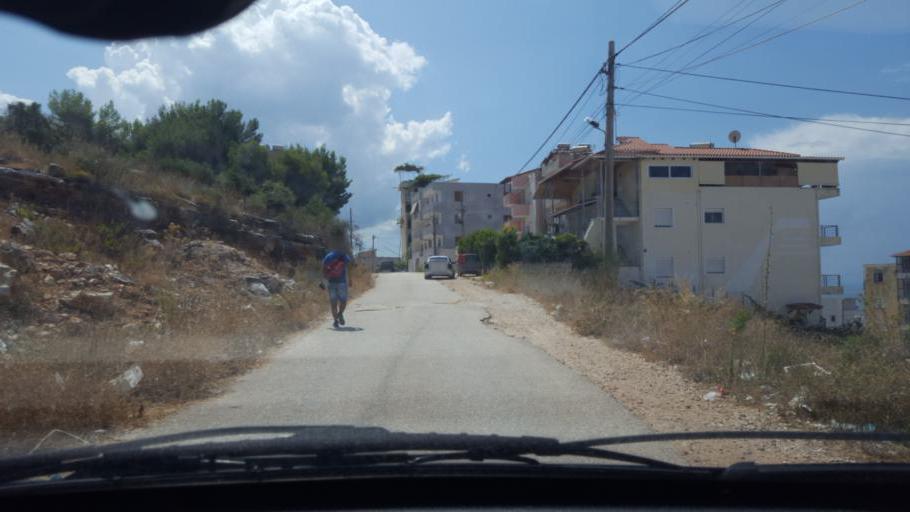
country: AL
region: Vlore
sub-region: Rrethi i Sarandes
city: Sarande
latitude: 39.8661
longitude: 20.0195
